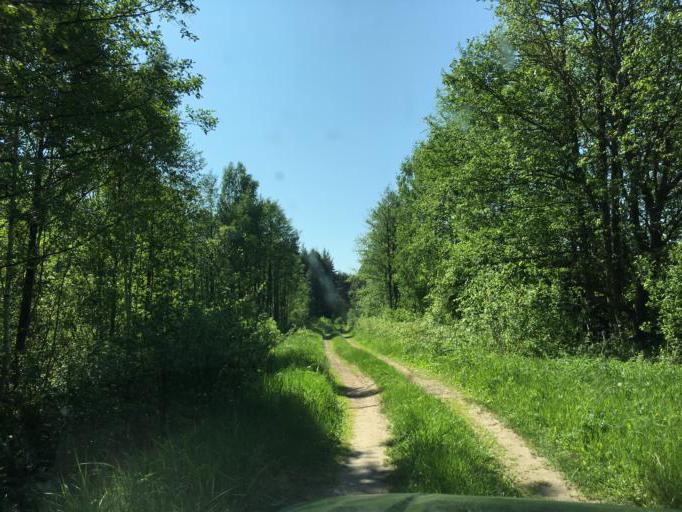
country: LV
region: Ventspils
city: Ventspils
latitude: 57.4767
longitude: 21.7633
